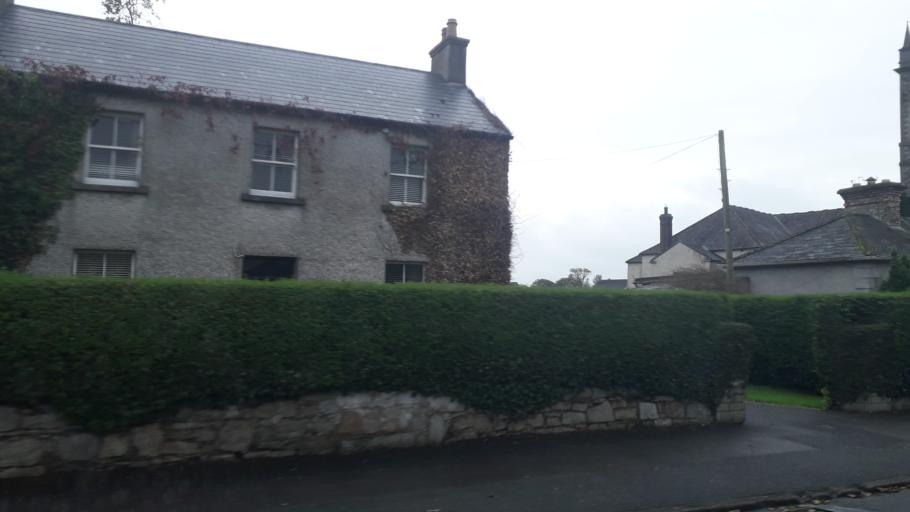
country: IE
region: Leinster
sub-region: An Longfort
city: Longford
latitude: 53.7319
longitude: -7.8007
